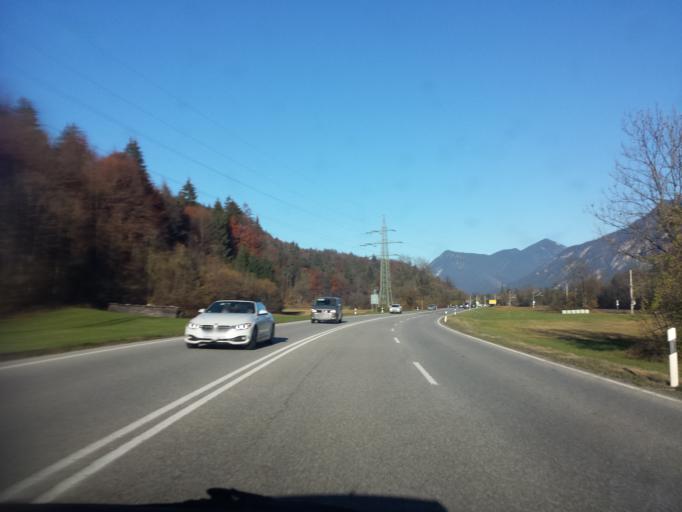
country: DE
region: Bavaria
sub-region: Upper Bavaria
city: Oberau
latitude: 47.5471
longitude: 11.1239
